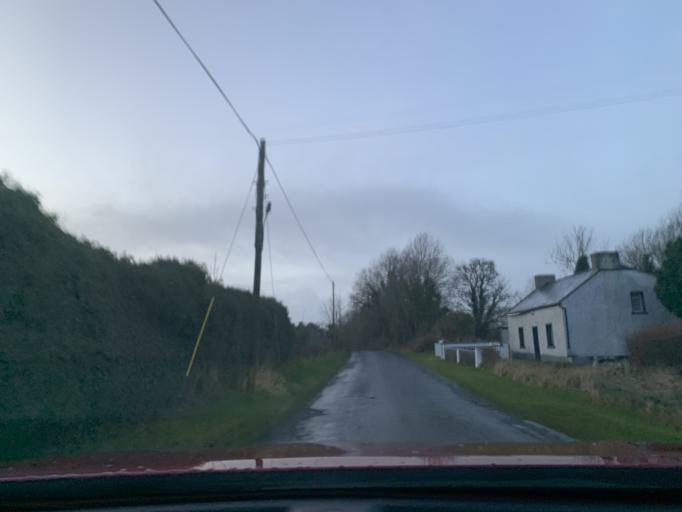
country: IE
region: Connaught
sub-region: Sligo
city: Ballymote
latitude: 54.1220
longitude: -8.5805
